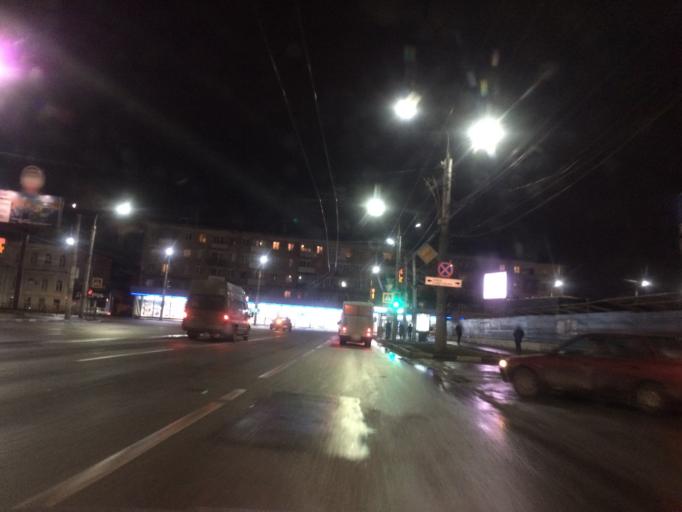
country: RU
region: Tula
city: Tula
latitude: 54.1962
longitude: 37.6105
